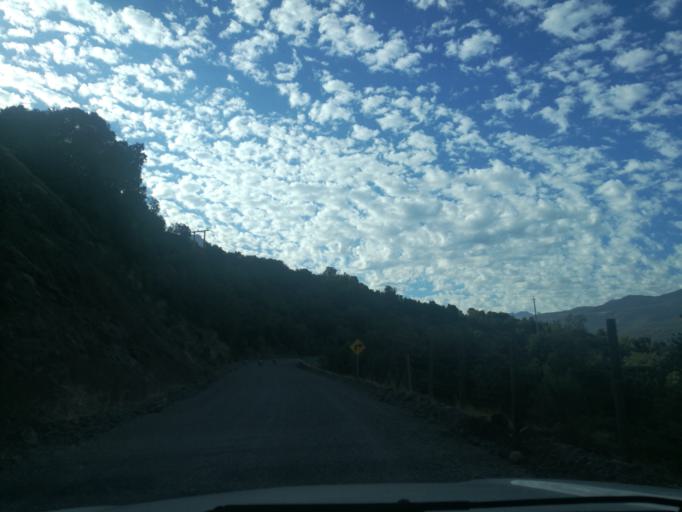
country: CL
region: O'Higgins
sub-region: Provincia de Cachapoal
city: Machali
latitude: -34.2490
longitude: -70.4669
